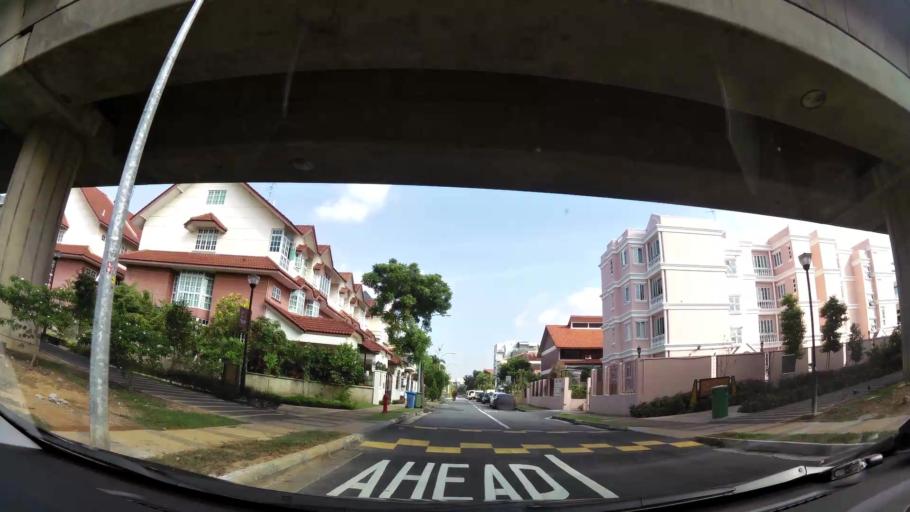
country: SG
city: Singapore
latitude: 1.3201
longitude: 103.9093
